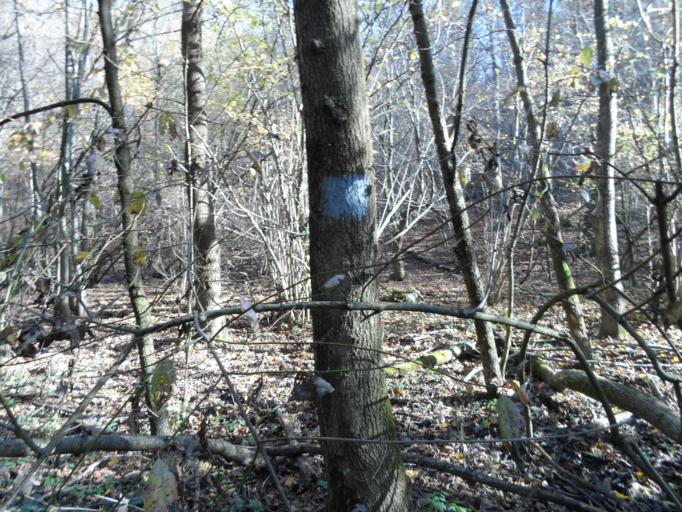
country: HU
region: Veszprem
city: Varpalota
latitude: 47.2511
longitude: 18.1107
